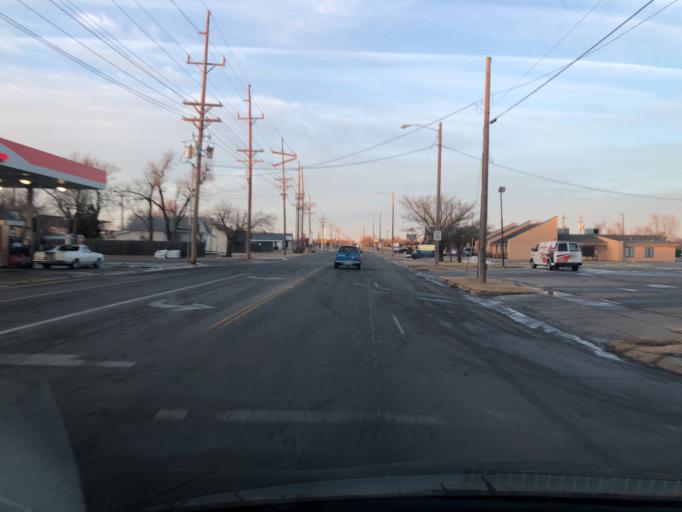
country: US
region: Kansas
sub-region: Reno County
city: Hutchinson
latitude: 38.0720
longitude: -97.9221
